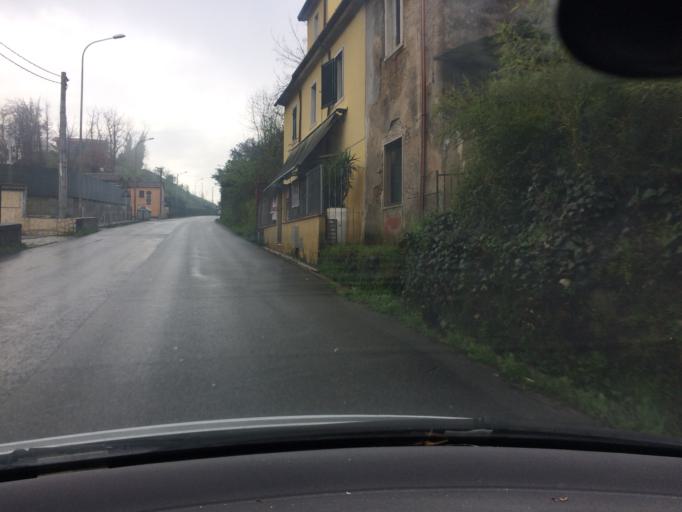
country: IT
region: Tuscany
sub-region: Provincia di Massa-Carrara
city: Massa
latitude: 44.0680
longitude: 10.1097
